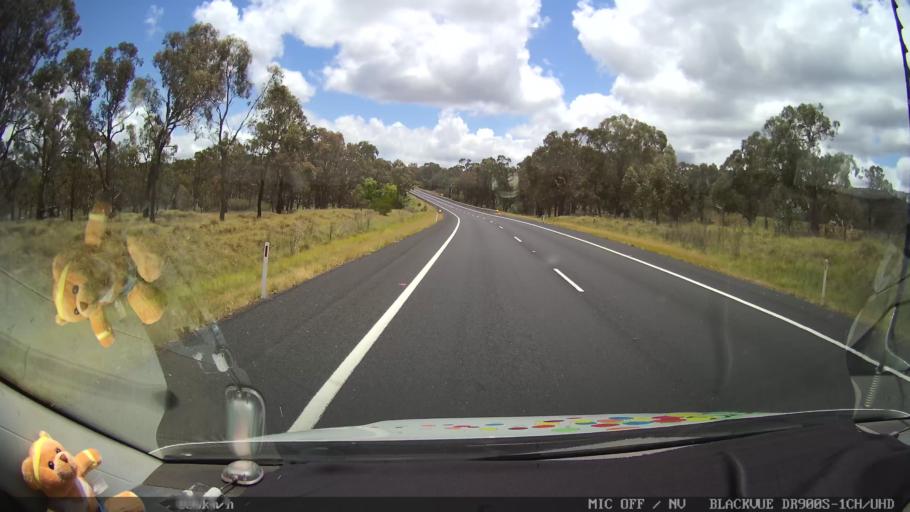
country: AU
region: New South Wales
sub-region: Glen Innes Severn
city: Glen Innes
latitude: -29.3614
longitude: 151.8988
